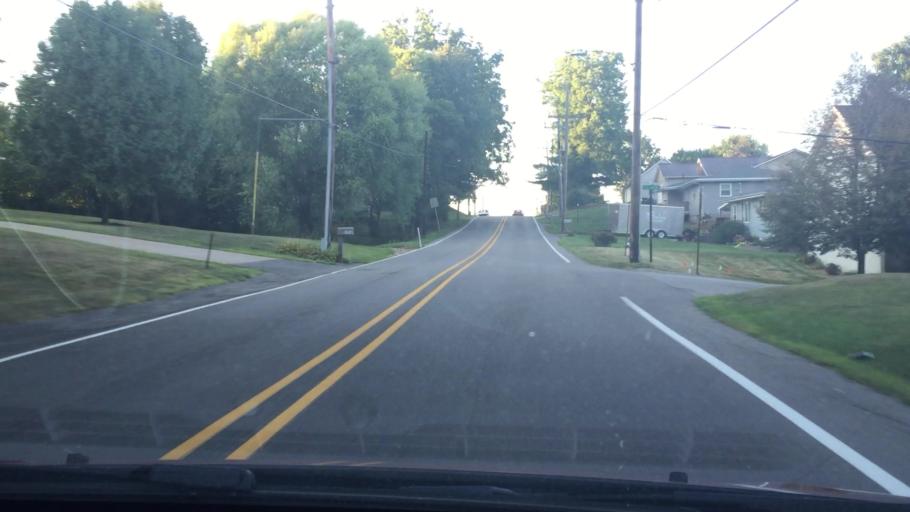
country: US
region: Iowa
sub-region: Muscatine County
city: Muscatine
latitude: 41.4294
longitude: -91.0649
